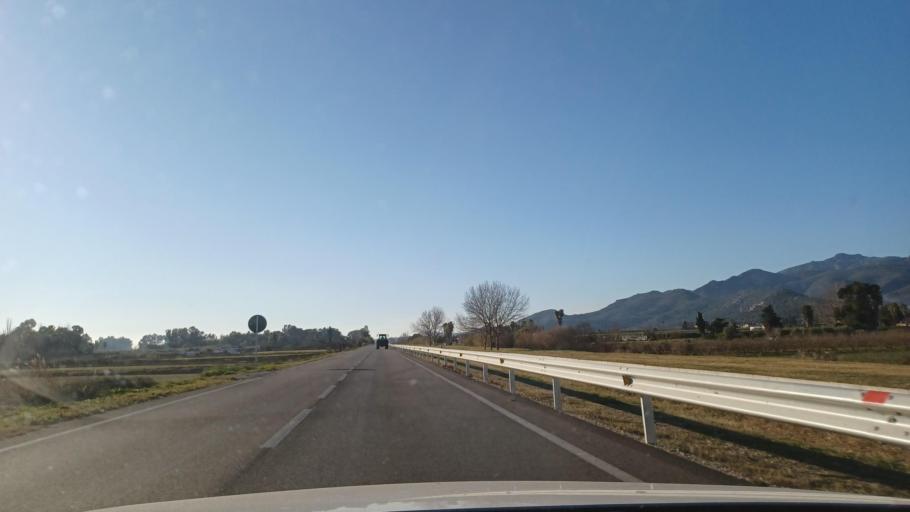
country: ES
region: Catalonia
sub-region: Provincia de Tarragona
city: Amposta
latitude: 40.6808
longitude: 0.5905
